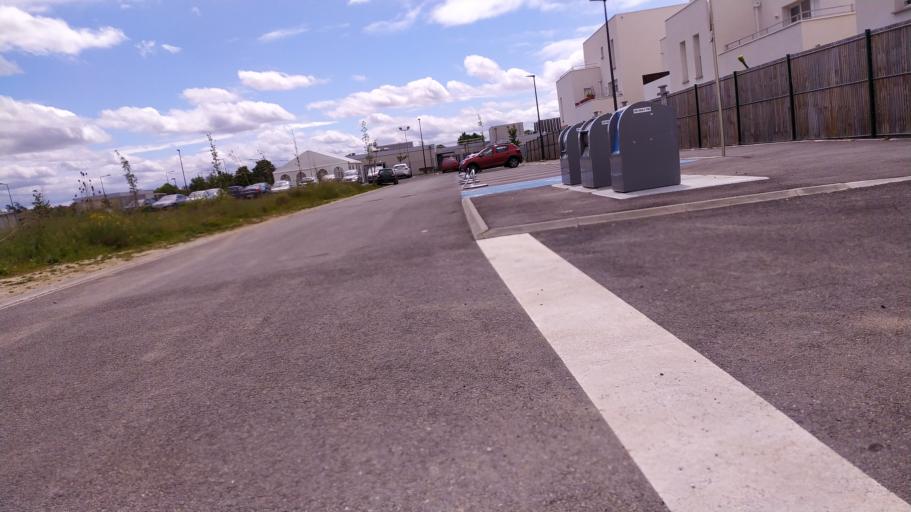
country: FR
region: Midi-Pyrenees
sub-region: Departement de la Haute-Garonne
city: La Salvetat-Saint-Gilles
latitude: 43.5841
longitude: 1.2839
